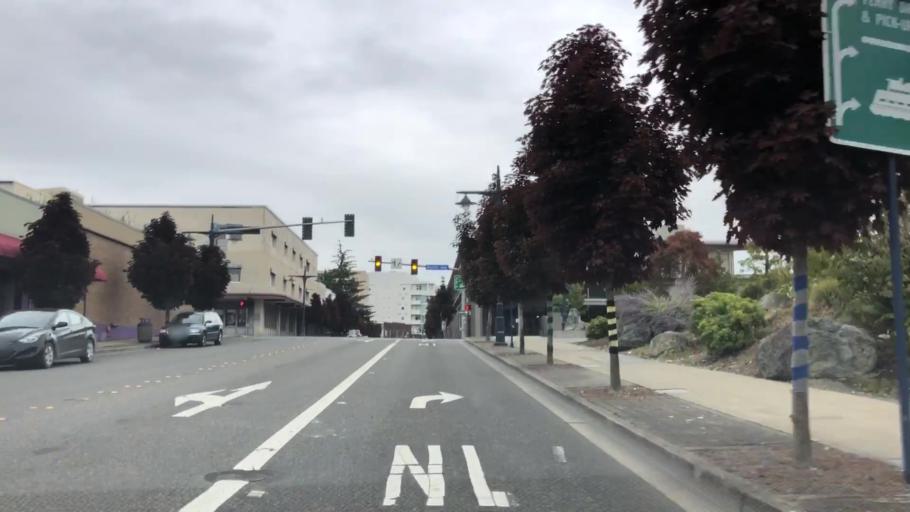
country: US
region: Washington
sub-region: Kitsap County
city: Bremerton
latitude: 47.5650
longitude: -122.6277
